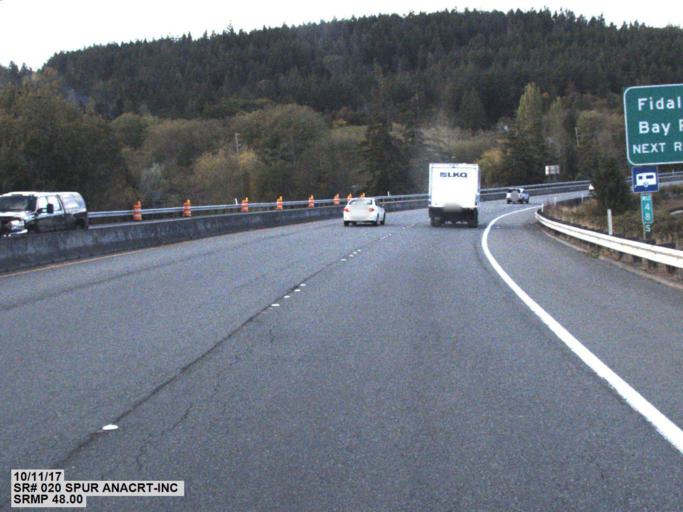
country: US
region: Washington
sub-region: Jefferson County
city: Port Hadlock-Irondale
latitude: 47.9880
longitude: -122.8845
